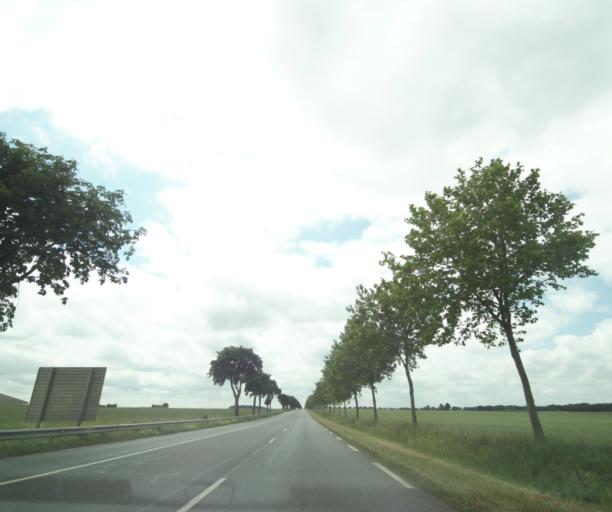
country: FR
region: Poitou-Charentes
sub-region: Departement des Deux-Sevres
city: Saint-Jean-de-Thouars
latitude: 46.9537
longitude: -0.2070
